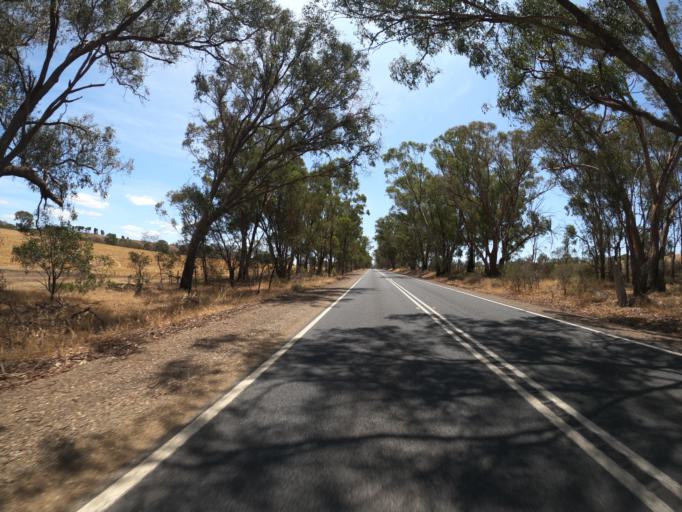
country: AU
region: Victoria
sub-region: Benalla
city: Benalla
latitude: -36.3748
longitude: 145.9742
